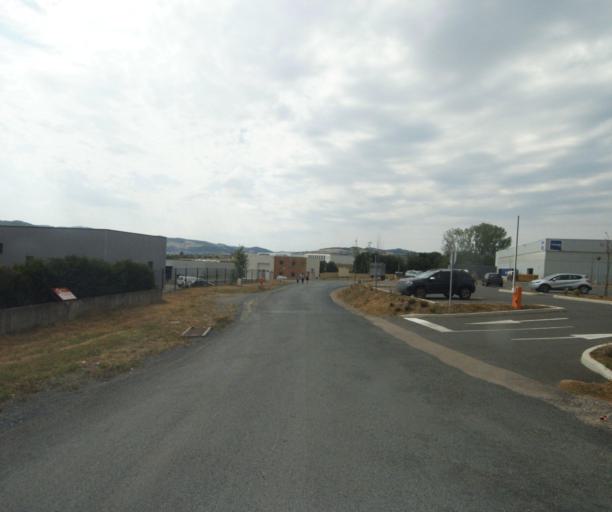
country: FR
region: Rhone-Alpes
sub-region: Departement du Rhone
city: Saint-Romain-de-Popey
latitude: 45.8794
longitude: 4.5410
